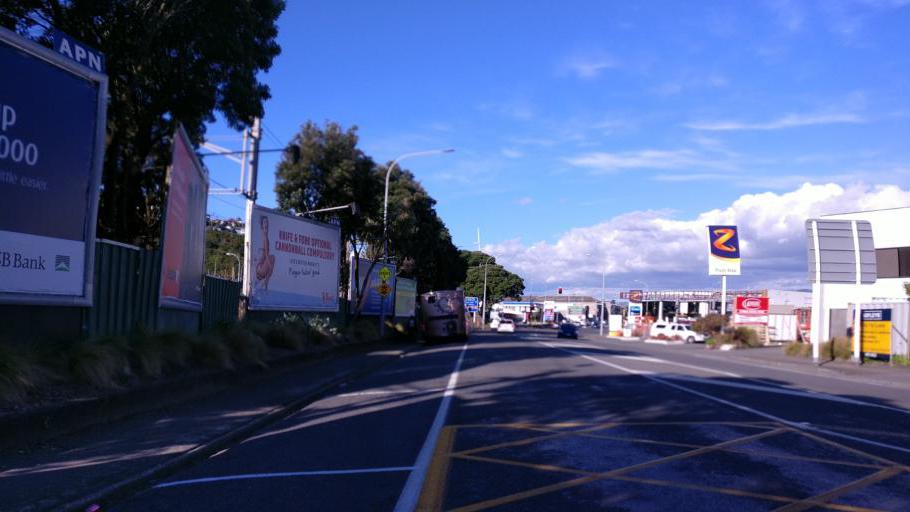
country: NZ
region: Wellington
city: Petone
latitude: -41.2230
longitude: 174.8677
